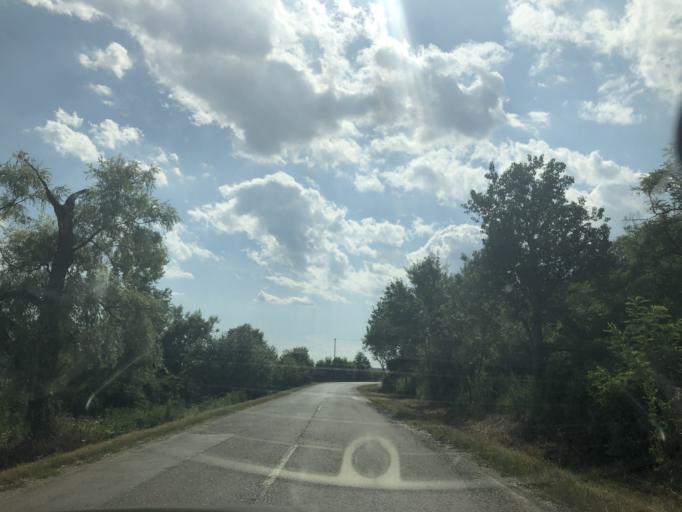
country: HU
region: Borsod-Abauj-Zemplen
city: Szendro
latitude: 48.4566
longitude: 20.7853
